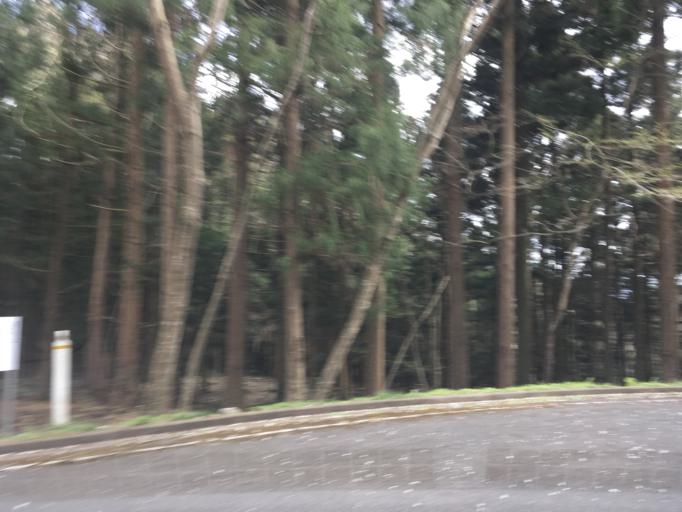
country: JP
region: Iwate
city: Ichinoseki
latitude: 38.7509
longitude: 141.2735
